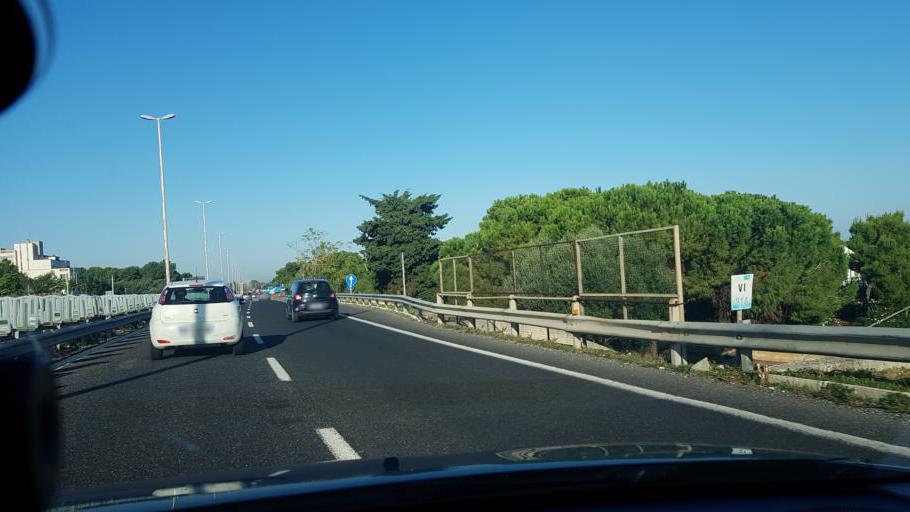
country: IT
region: Apulia
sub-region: Provincia di Bari
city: Parco Scizzo-Parchitello
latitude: 41.0826
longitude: 17.0047
